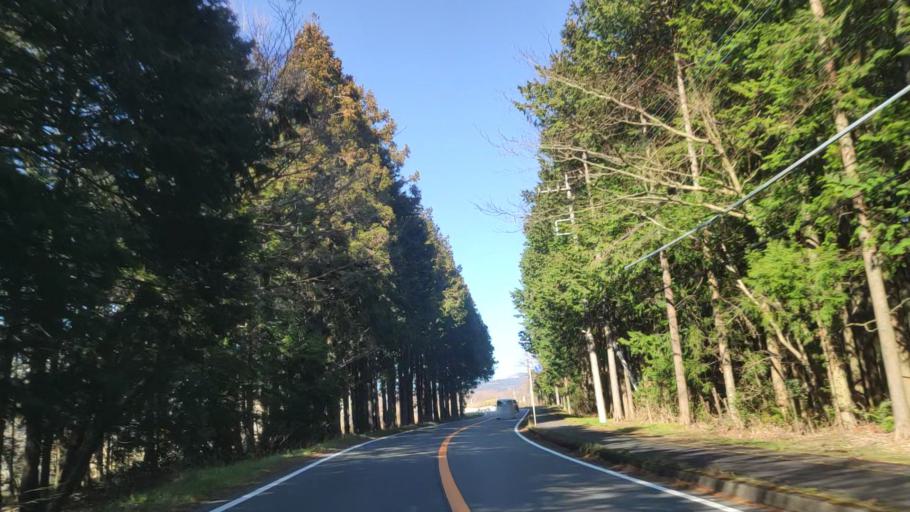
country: JP
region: Shizuoka
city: Fujinomiya
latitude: 35.3268
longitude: 138.5930
